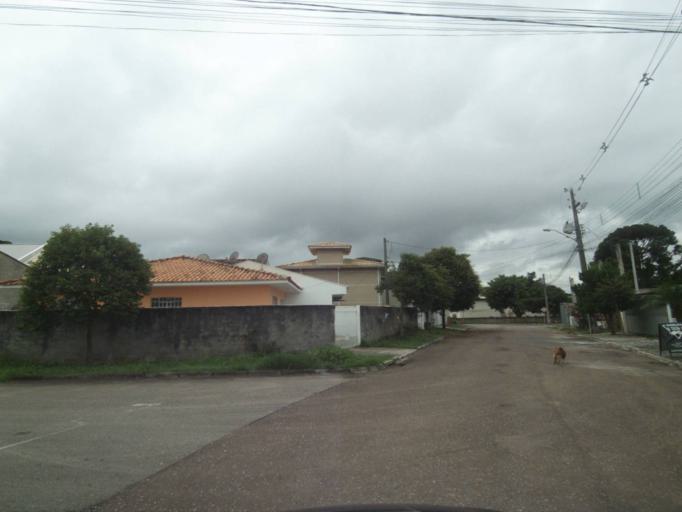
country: BR
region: Parana
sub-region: Curitiba
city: Curitiba
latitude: -25.4674
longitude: -49.3224
